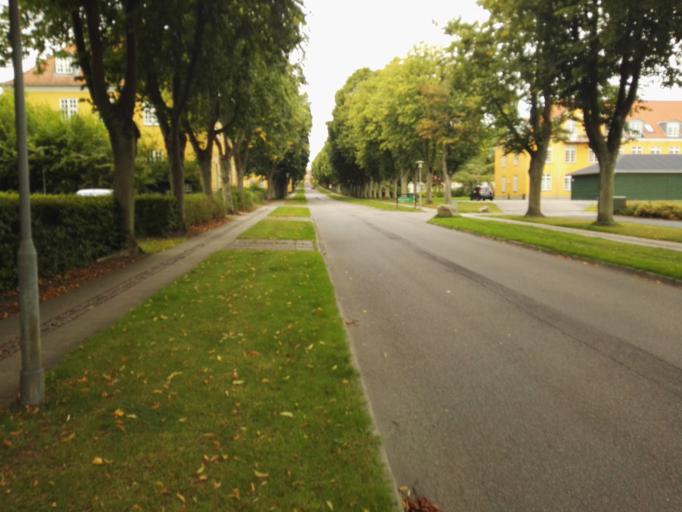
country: DK
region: Zealand
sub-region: Odsherred Kommune
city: Nykobing Sjaelland
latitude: 55.9079
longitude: 11.6662
